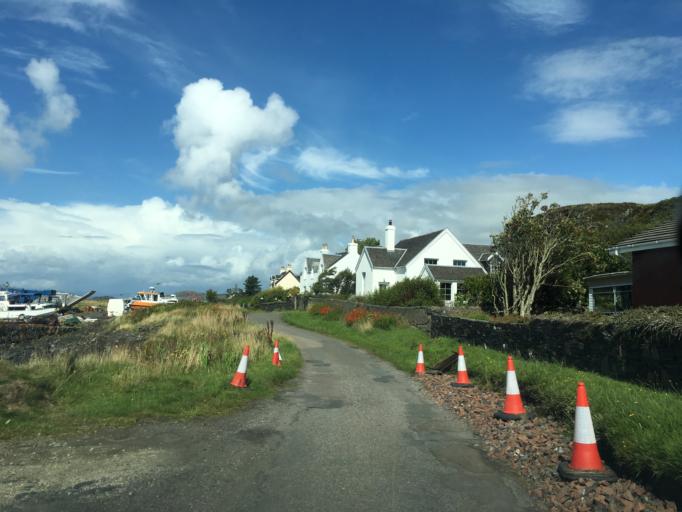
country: GB
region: Scotland
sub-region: Argyll and Bute
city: Isle Of Mull
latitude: 56.2508
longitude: -5.6542
